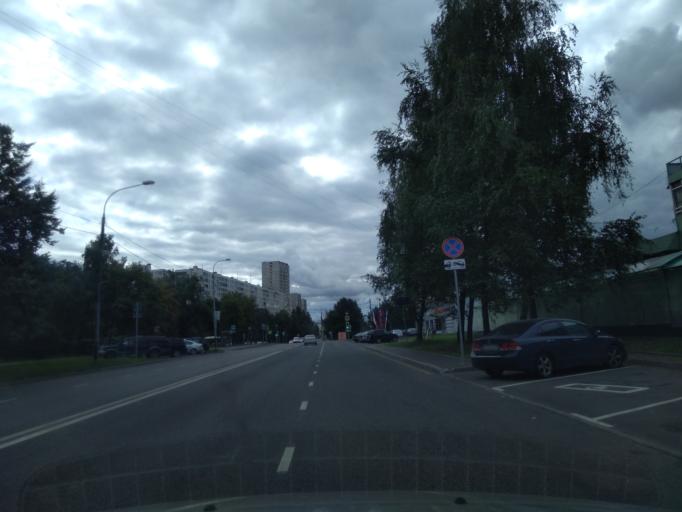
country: RU
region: Moscow
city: Strogino
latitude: 55.8148
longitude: 37.3931
